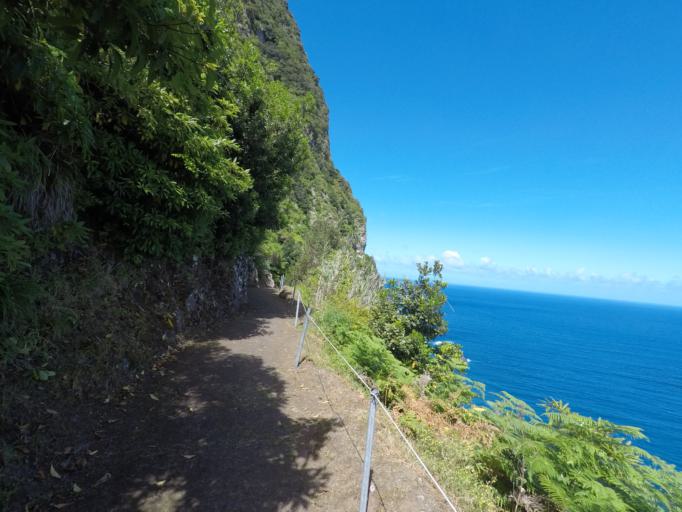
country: PT
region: Madeira
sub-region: Santana
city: Santana
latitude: 32.8257
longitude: -16.9637
